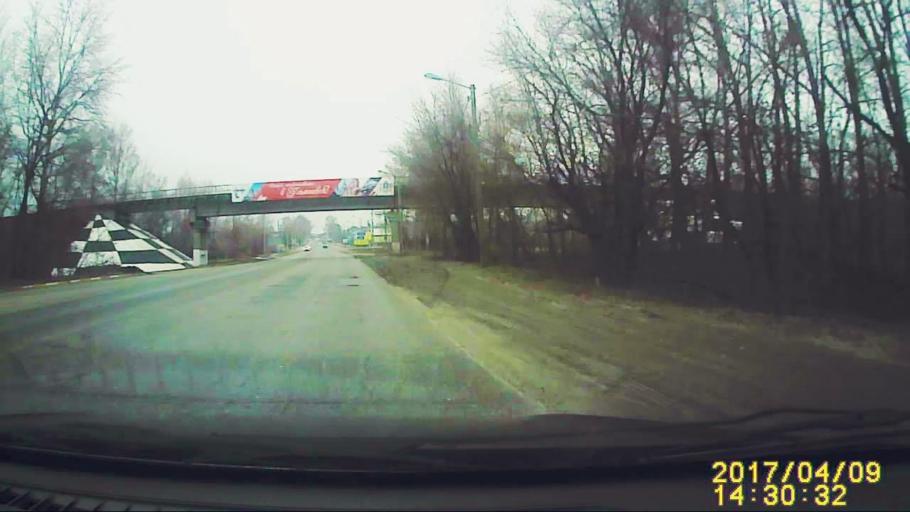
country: RU
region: Ulyanovsk
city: Novoul'yanovsk
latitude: 54.2141
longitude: 48.2977
